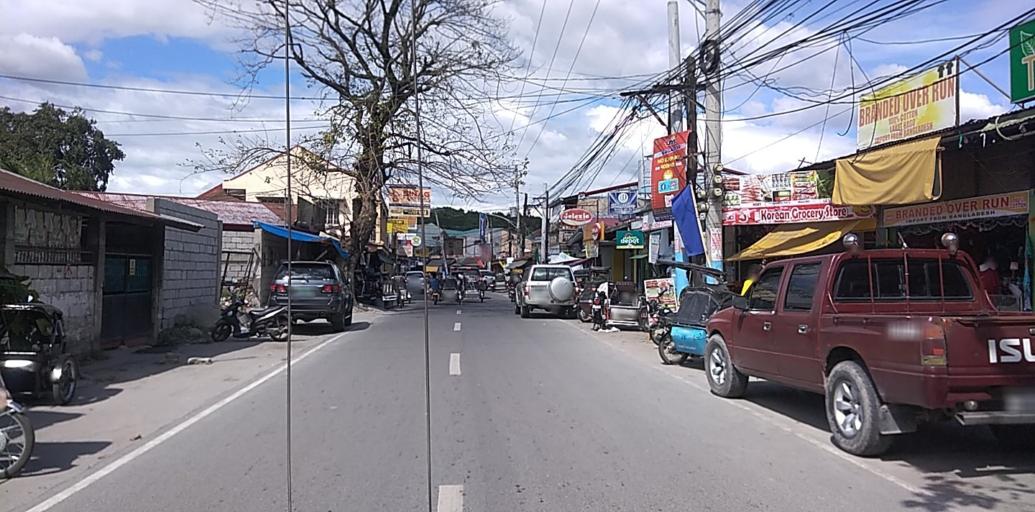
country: PH
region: Central Luzon
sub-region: Province of Pampanga
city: Porac
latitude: 15.0703
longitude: 120.5435
